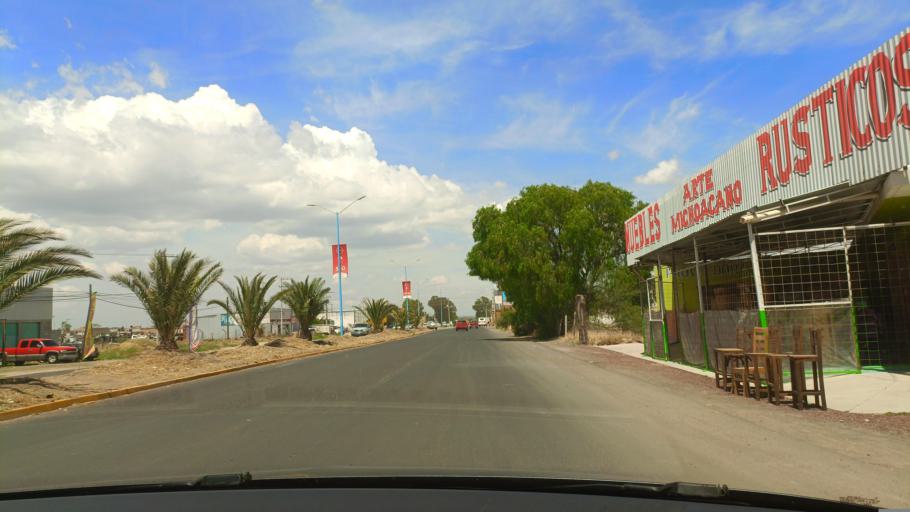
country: MX
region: Guanajuato
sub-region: San Luis de la Paz
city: San Ignacio
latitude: 21.2944
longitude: -100.5342
